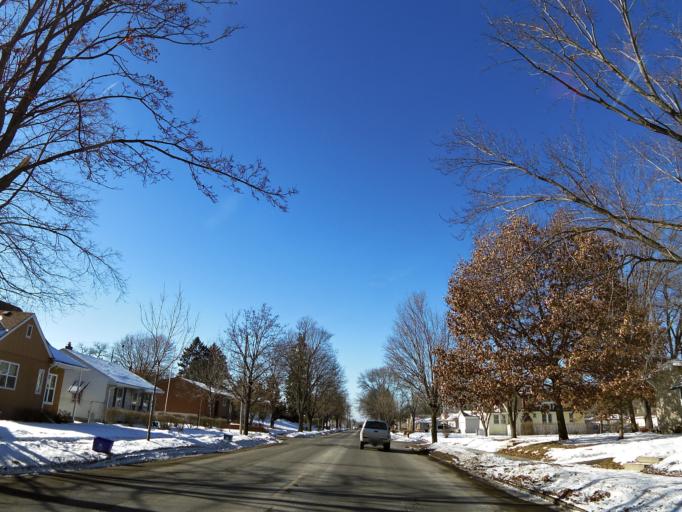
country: US
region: Minnesota
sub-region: Ramsey County
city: Maplewood
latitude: 44.9631
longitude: -93.0322
